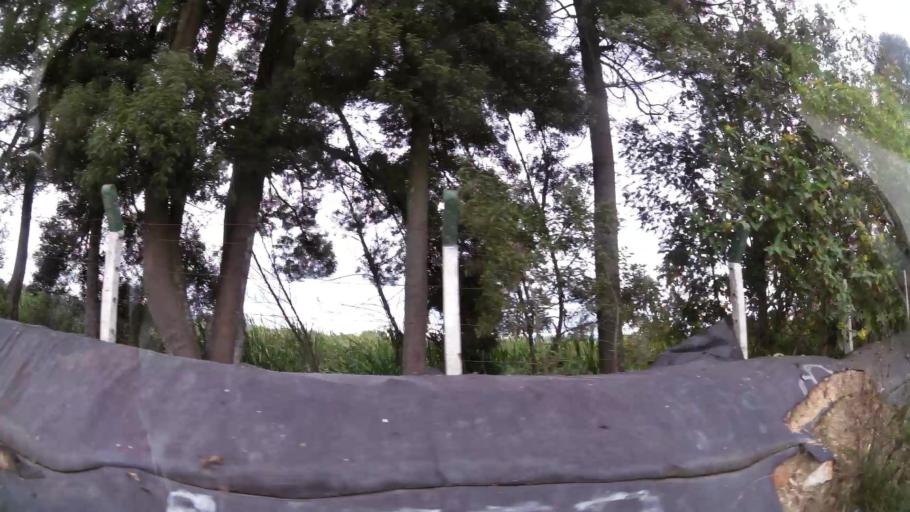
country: CO
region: Cundinamarca
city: Funza
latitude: 4.7230
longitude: -74.1458
